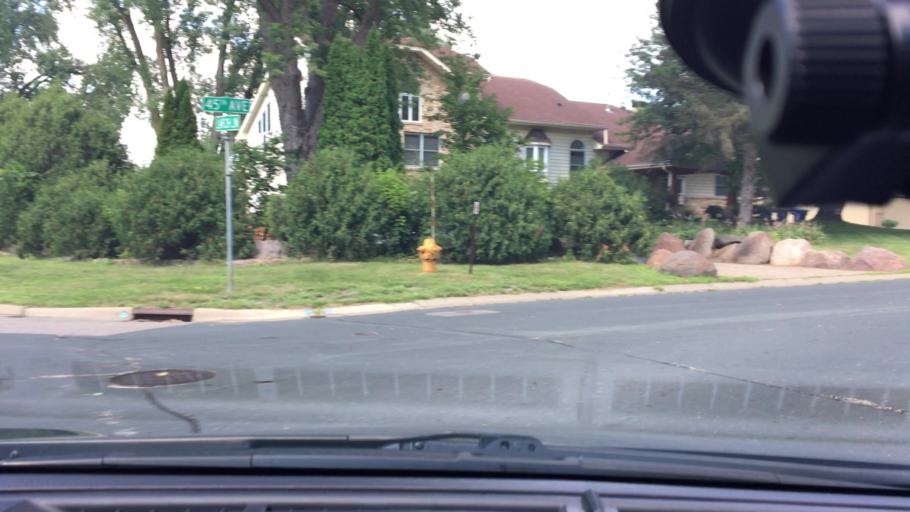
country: US
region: Minnesota
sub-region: Hennepin County
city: Plymouth
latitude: 45.0368
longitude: -93.4361
